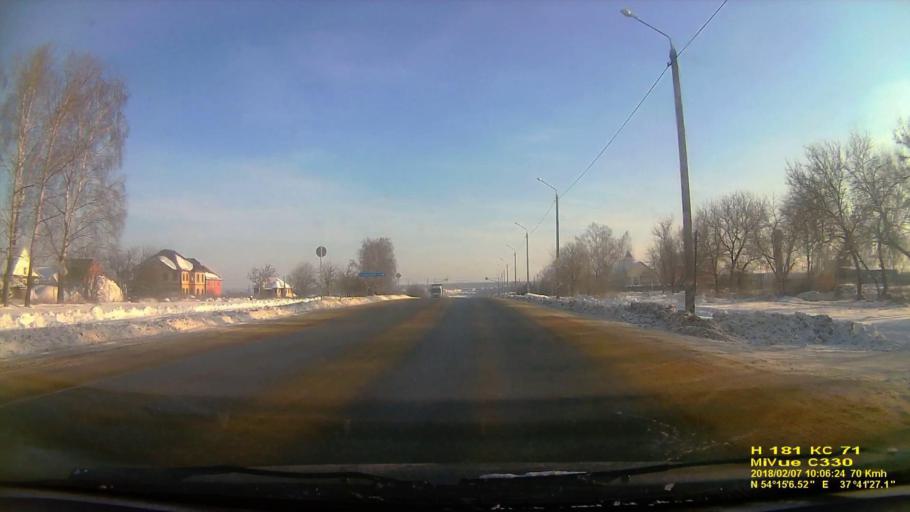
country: RU
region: Tula
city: Gorelki
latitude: 54.2520
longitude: 37.6915
